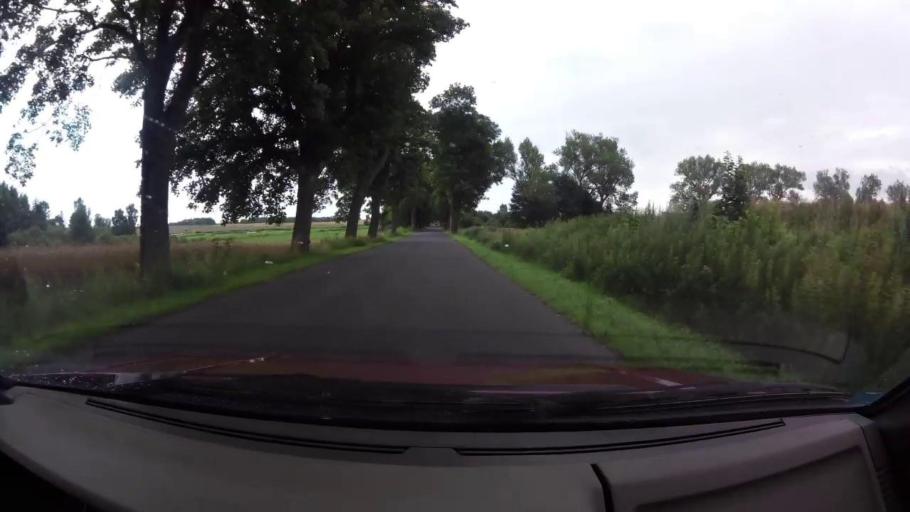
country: PL
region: West Pomeranian Voivodeship
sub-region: Koszalin
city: Koszalin
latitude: 54.1496
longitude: 16.1302
